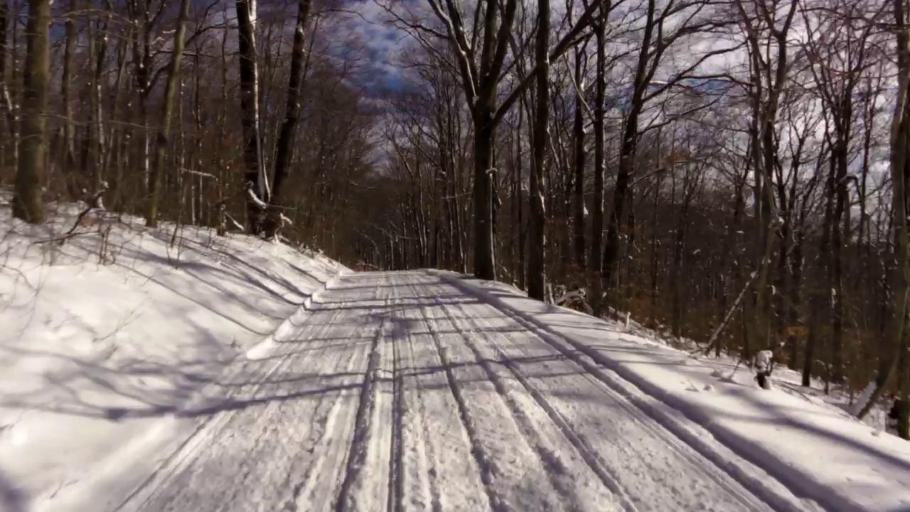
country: US
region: New York
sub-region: Cattaraugus County
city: Salamanca
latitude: 42.0705
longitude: -78.6775
